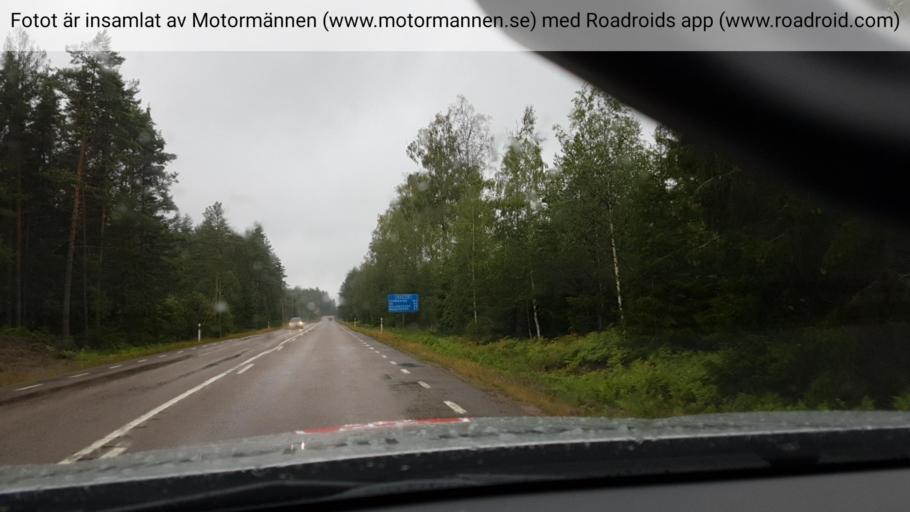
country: SE
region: Vaestra Goetaland
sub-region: Amals Kommun
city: Amal
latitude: 59.0737
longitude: 12.5663
